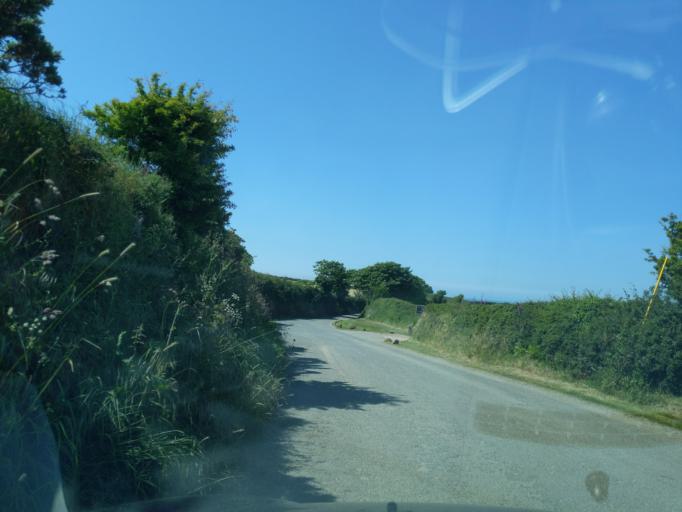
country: GB
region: England
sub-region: Cornwall
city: Wadebridge
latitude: 50.5758
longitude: -4.8297
